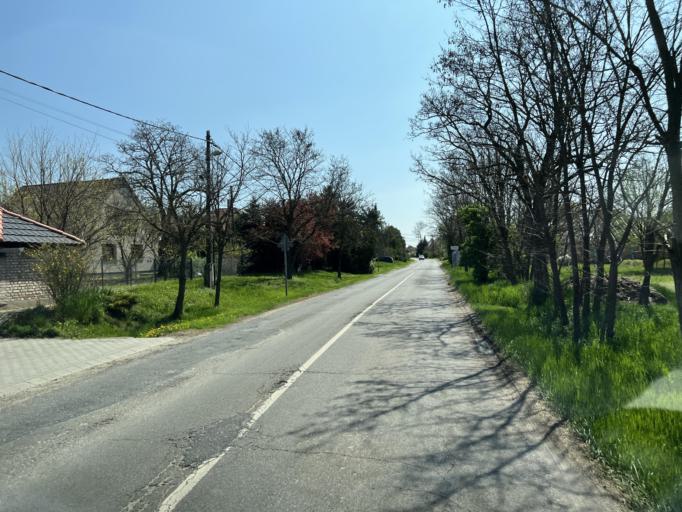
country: HU
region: Pest
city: Ocsa
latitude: 47.2988
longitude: 19.2144
